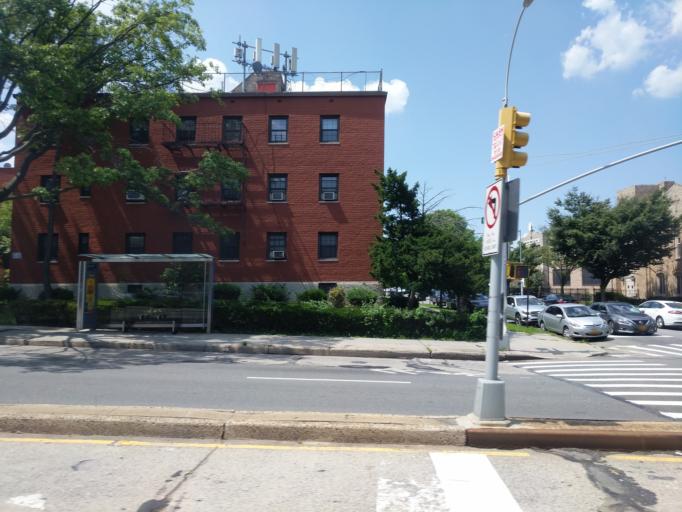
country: US
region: New York
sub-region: Queens County
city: Jamaica
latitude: 40.7205
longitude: -73.8184
